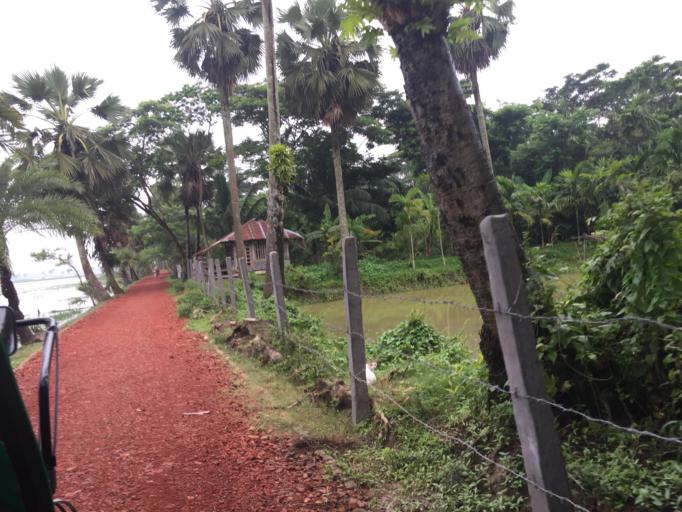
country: BD
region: Barisal
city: Mathba
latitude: 22.1970
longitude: 89.9342
